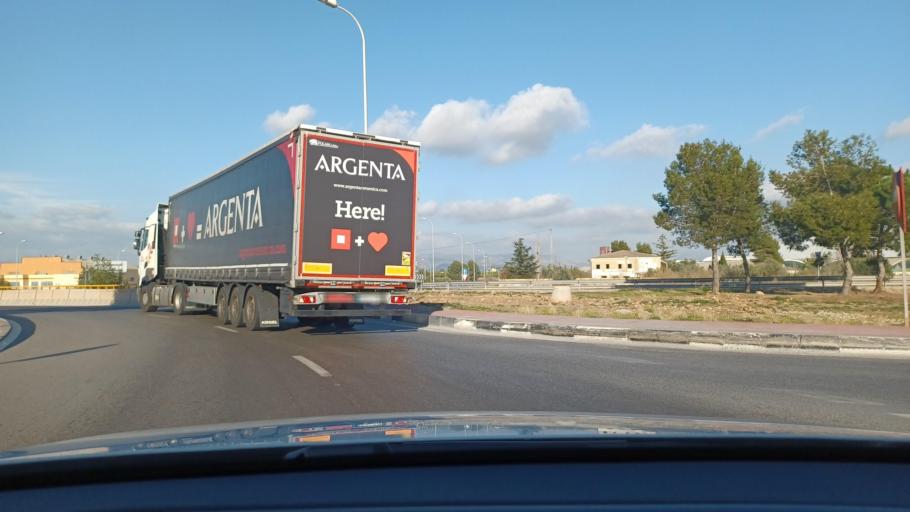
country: ES
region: Valencia
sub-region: Provincia de Castello
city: Betxi
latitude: 39.9494
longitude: -0.1787
